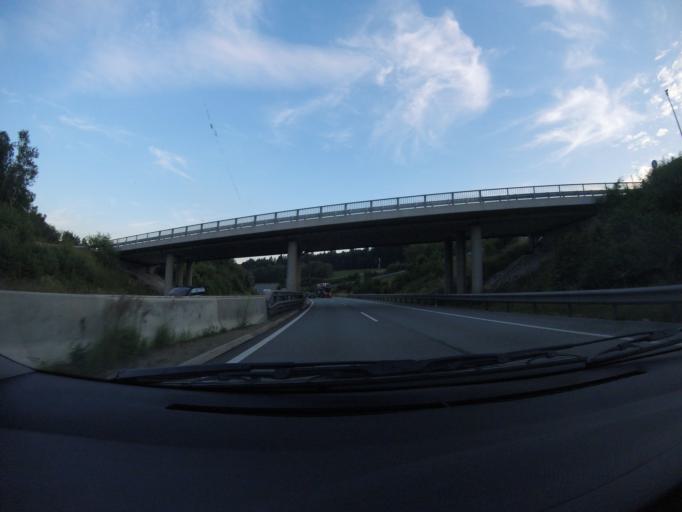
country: AT
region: Styria
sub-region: Politischer Bezirk Hartberg-Fuerstenfeld
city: Schaeffern
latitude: 47.4806
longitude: 16.0930
